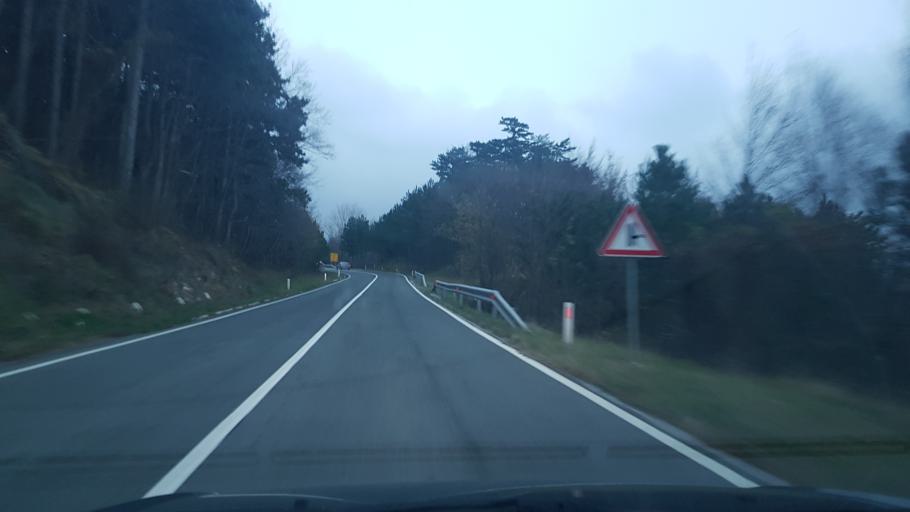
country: SI
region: Vipava
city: Vipava
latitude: 45.8788
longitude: 13.9636
